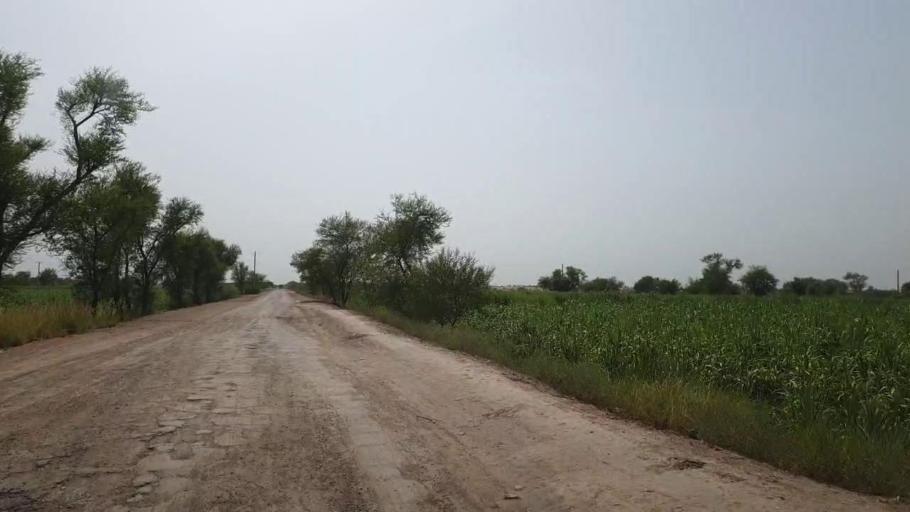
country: PK
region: Sindh
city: Bandhi
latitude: 26.5386
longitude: 68.4012
